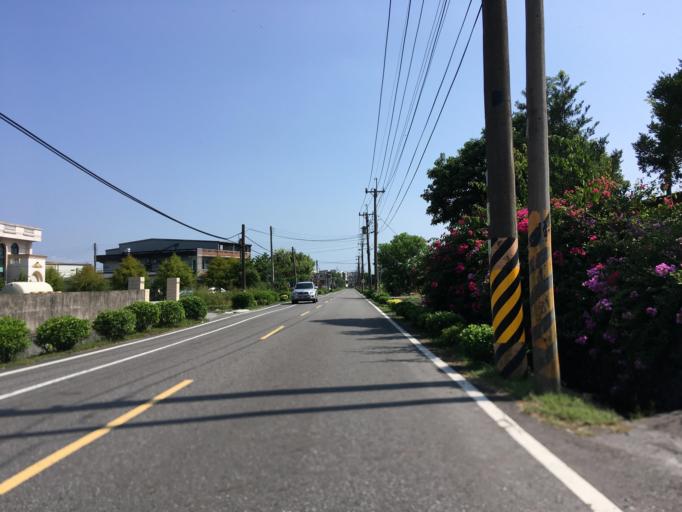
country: TW
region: Taiwan
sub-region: Yilan
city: Yilan
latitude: 24.6815
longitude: 121.7380
